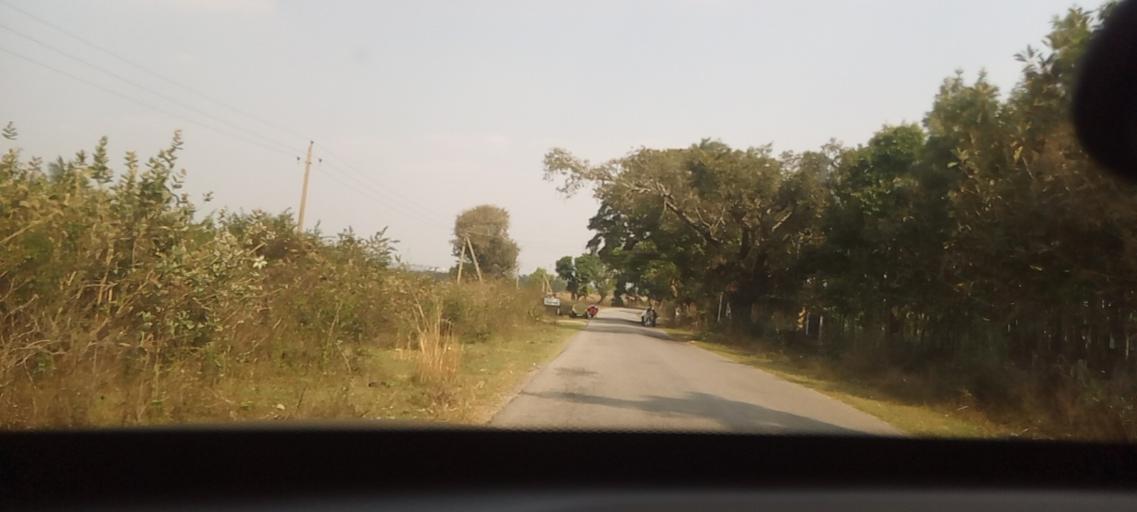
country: IN
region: Karnataka
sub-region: Hassan
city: Belur
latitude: 13.1820
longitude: 75.8400
